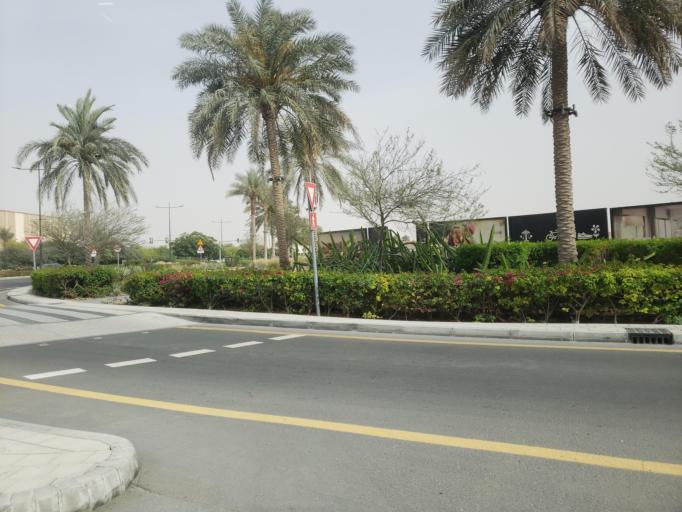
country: AE
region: Dubai
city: Dubai
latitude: 25.0038
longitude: 55.2945
